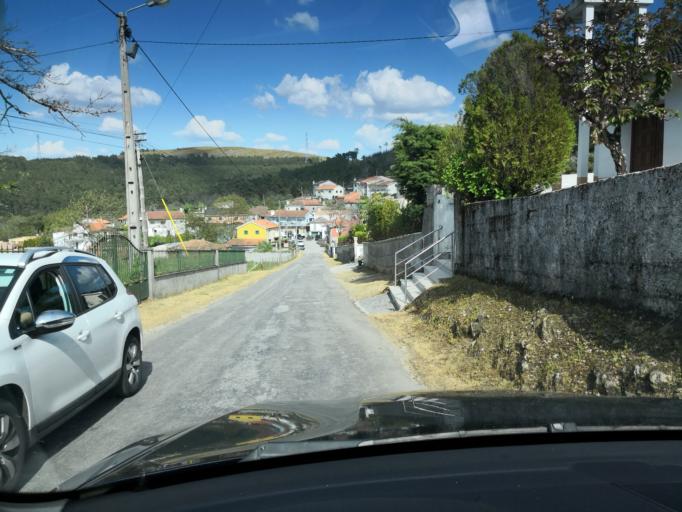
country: PT
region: Vila Real
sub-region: Sabrosa
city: Vilela
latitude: 41.2377
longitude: -7.6793
